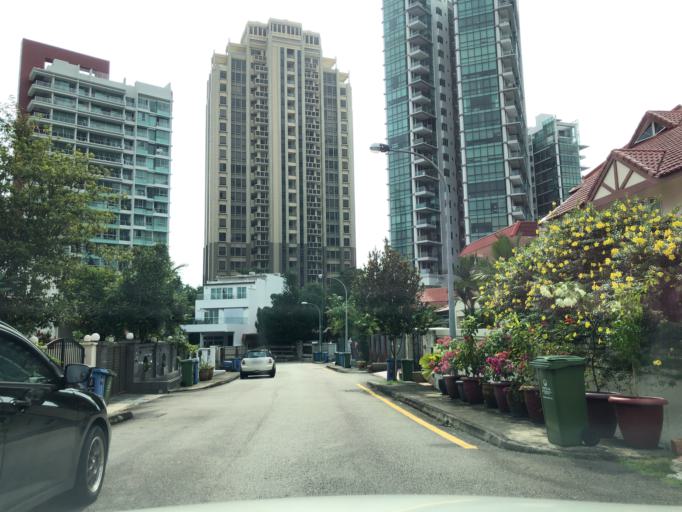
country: SG
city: Singapore
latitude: 1.3018
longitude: 103.8253
